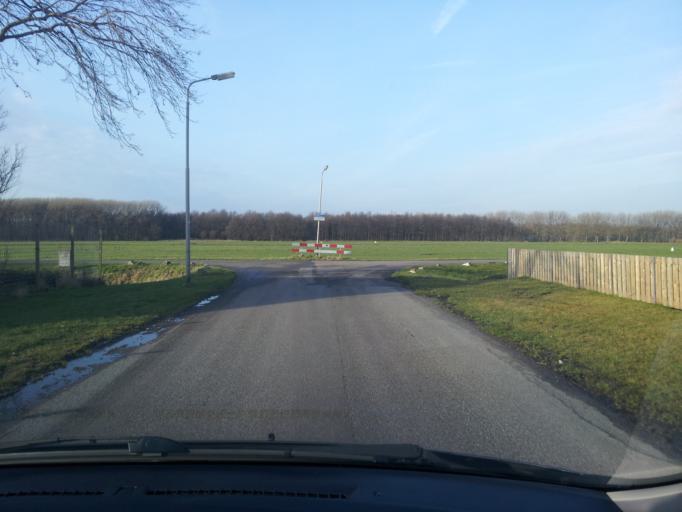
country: NL
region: South Holland
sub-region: Gemeente Pijnacker-Nootdorp
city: Pijnacker
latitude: 52.0173
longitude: 4.3976
